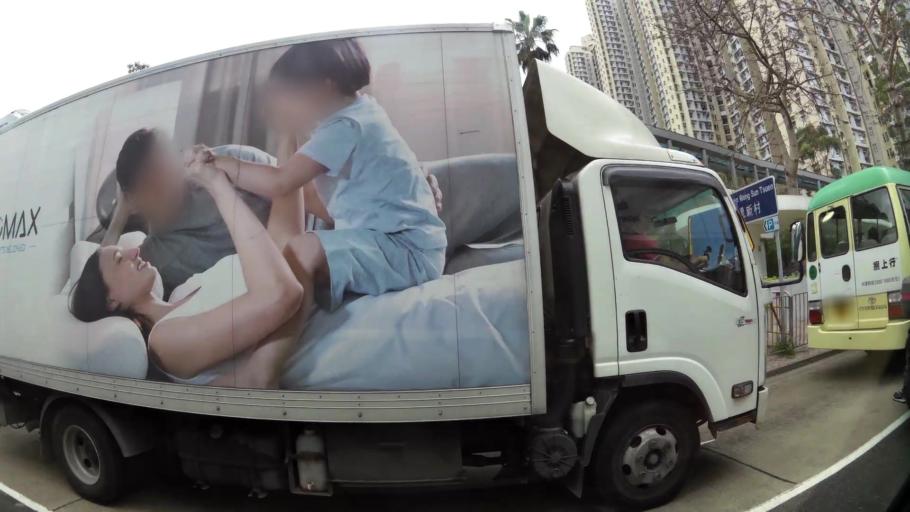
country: HK
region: Wong Tai Sin
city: Wong Tai Sin
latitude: 22.3469
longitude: 114.2041
